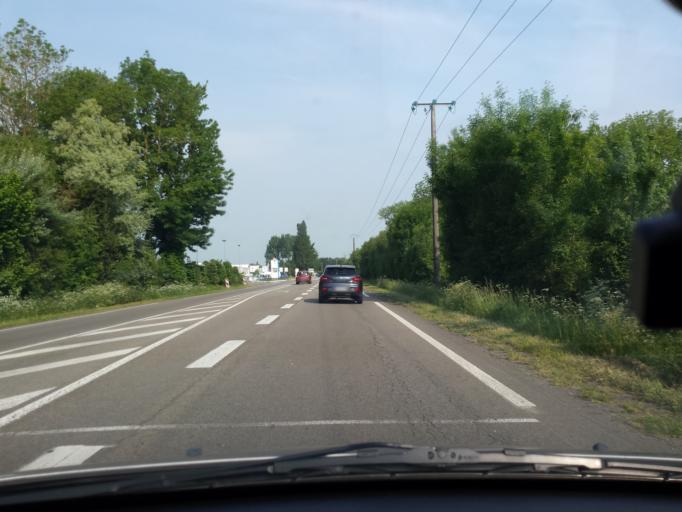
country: FR
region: Pays de la Loire
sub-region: Departement de la Loire-Atlantique
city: Machecoul
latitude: 46.9979
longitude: -1.8133
